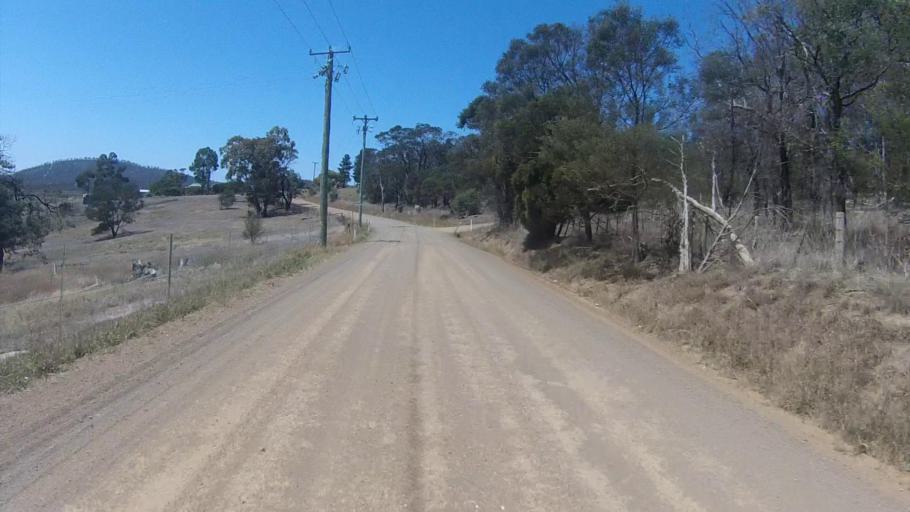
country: AU
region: Tasmania
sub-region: Sorell
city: Sorell
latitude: -42.8223
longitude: 147.6375
